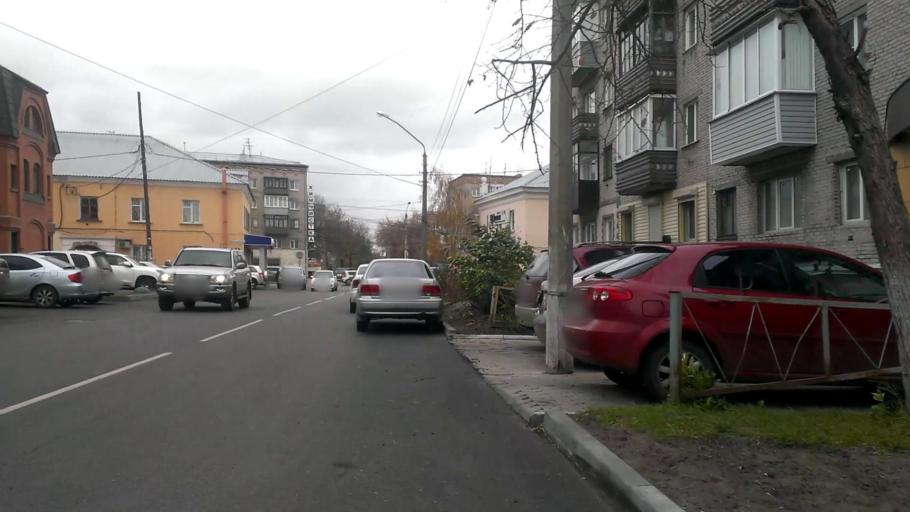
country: RU
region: Altai Krai
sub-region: Gorod Barnaulskiy
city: Barnaul
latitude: 53.3527
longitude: 83.7680
